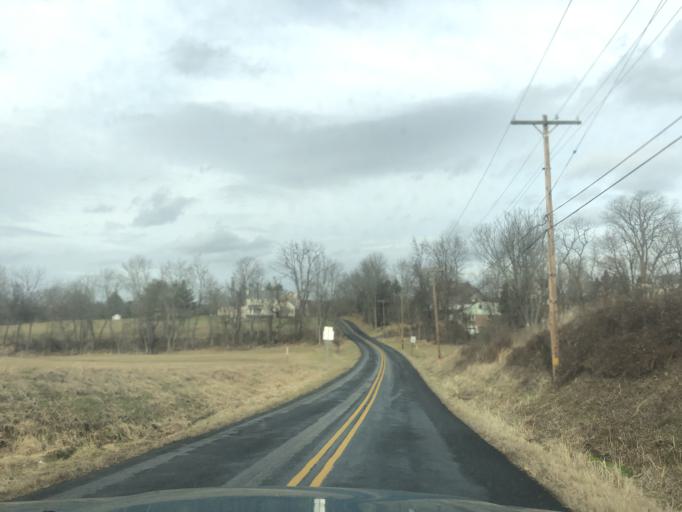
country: US
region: Pennsylvania
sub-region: Montgomery County
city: Harleysville
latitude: 40.2702
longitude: -75.4098
